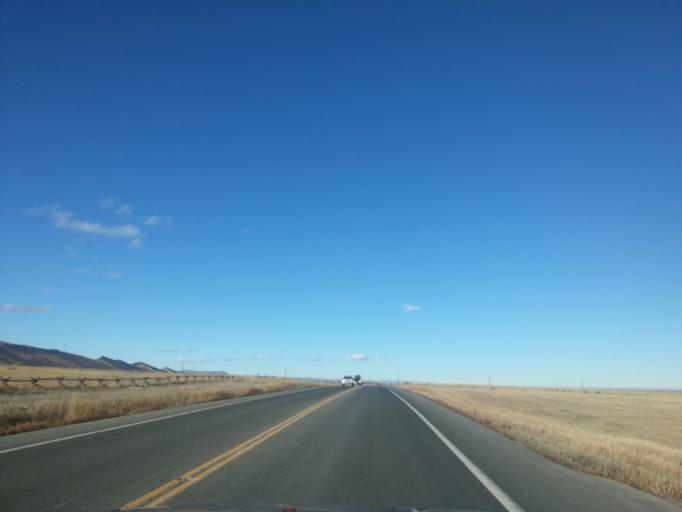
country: US
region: Colorado
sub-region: Larimer County
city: Loveland
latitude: 40.4871
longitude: -105.1156
